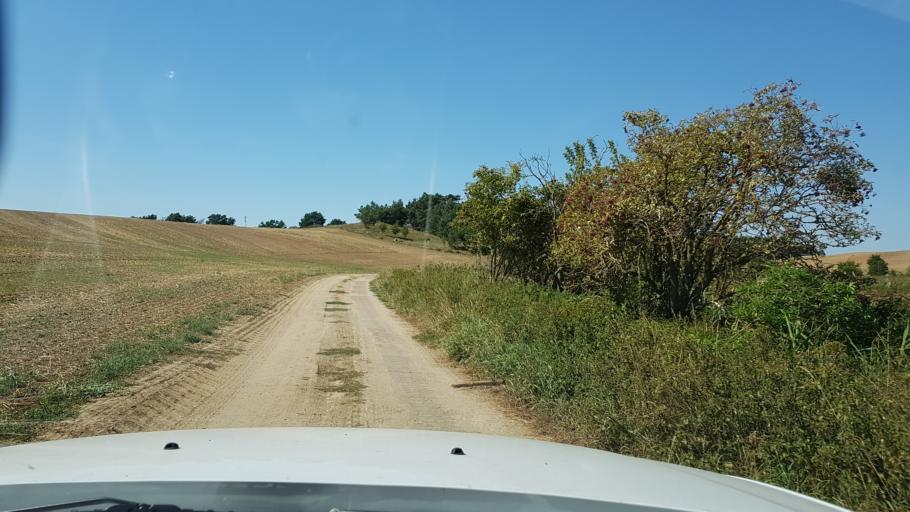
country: PL
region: West Pomeranian Voivodeship
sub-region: Powiat gryfinski
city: Moryn
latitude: 52.8482
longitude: 14.3610
